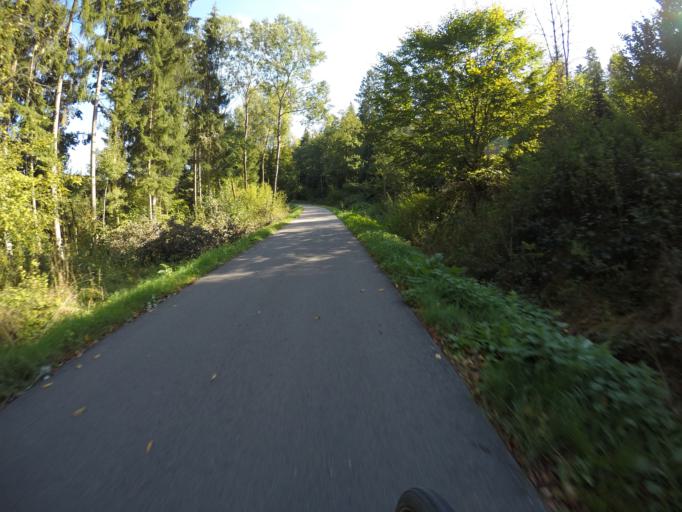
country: DE
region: Baden-Wuerttemberg
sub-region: Regierungsbezirk Stuttgart
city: Waldenbuch
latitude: 48.6622
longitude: 9.1455
